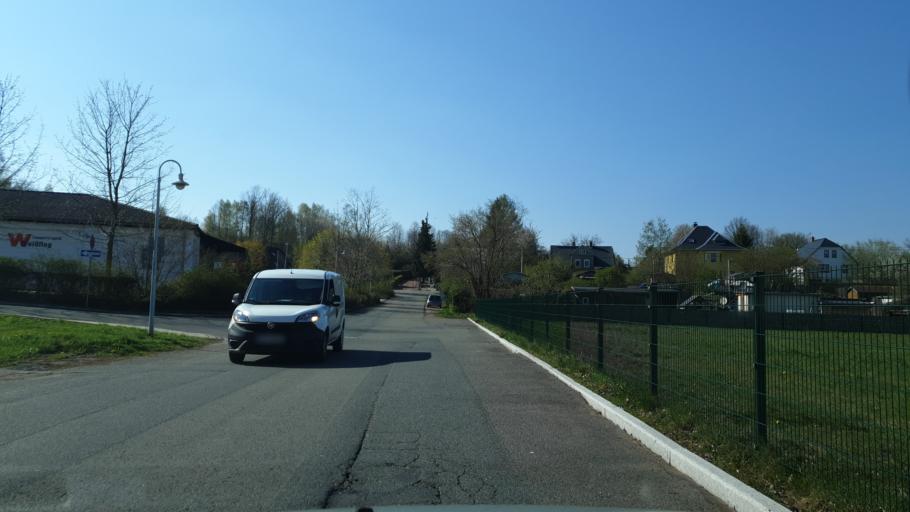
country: DE
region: Saxony
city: Oelsnitz
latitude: 50.7302
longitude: 12.7016
